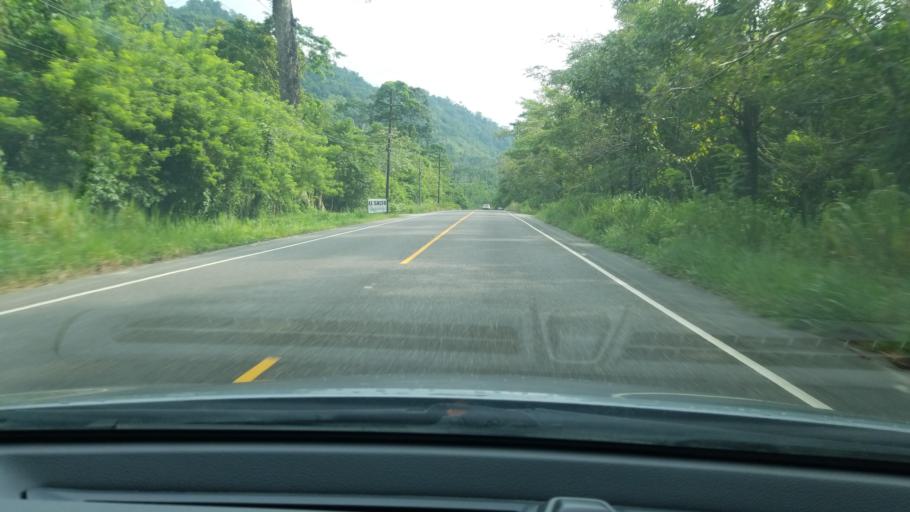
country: HN
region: Cortes
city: Potrerillos
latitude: 15.5998
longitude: -88.2976
